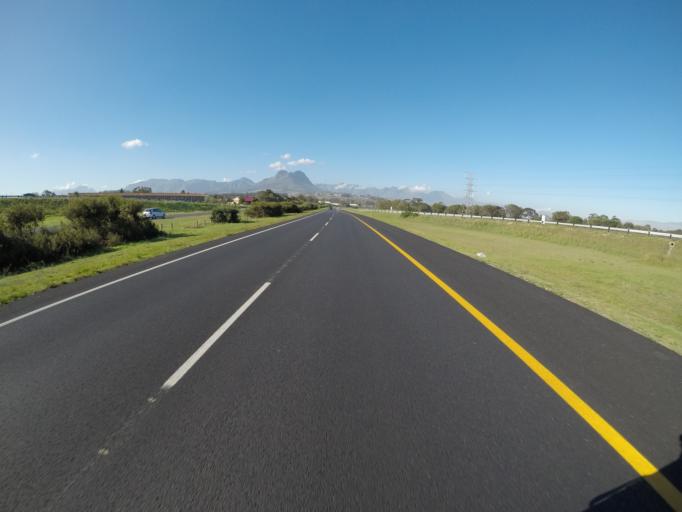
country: ZA
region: Western Cape
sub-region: Cape Winelands District Municipality
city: Stellenbosch
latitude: -34.0595
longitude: 18.7822
